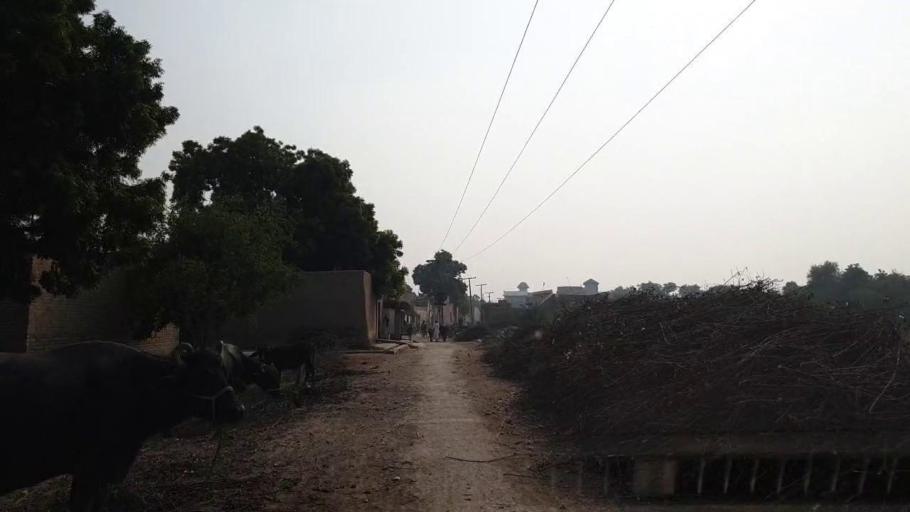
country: PK
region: Sindh
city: Bhan
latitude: 26.5808
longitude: 67.7301
